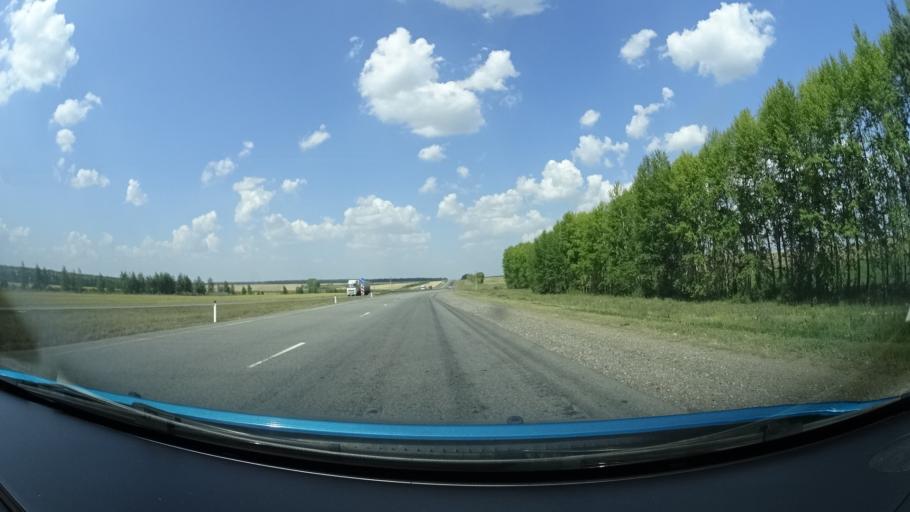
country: RU
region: Bashkortostan
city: Alekseyevka
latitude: 54.7261
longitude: 55.1576
